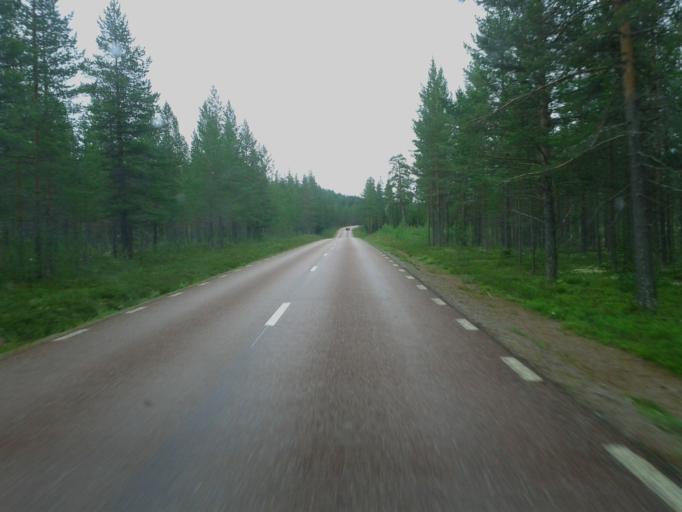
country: NO
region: Hedmark
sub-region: Trysil
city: Innbygda
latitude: 61.8025
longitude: 12.9131
